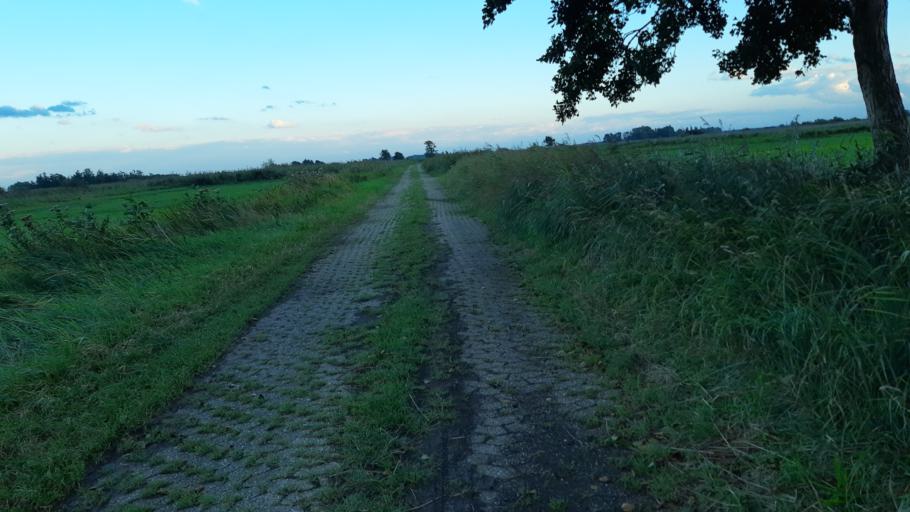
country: NL
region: Overijssel
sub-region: Gemeente Steenwijkerland
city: Blokzijl
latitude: 52.7377
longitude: 5.9844
